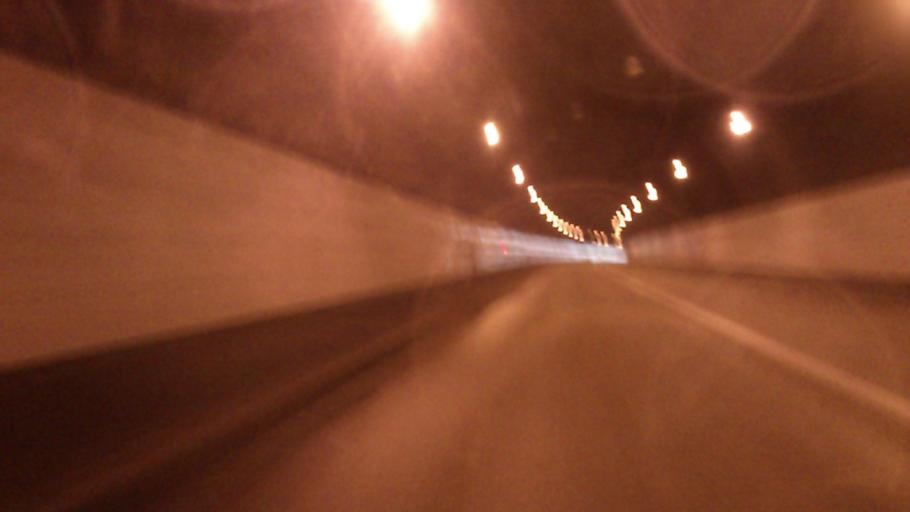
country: JP
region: Akita
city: Takanosu
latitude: 40.2168
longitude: 140.2330
